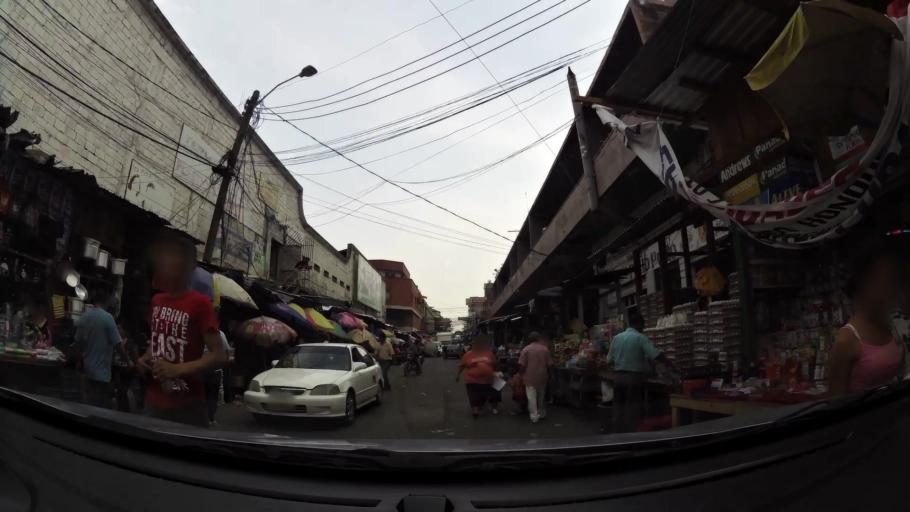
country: HN
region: Francisco Morazan
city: Tegucigalpa
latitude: 14.1021
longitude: -87.2096
